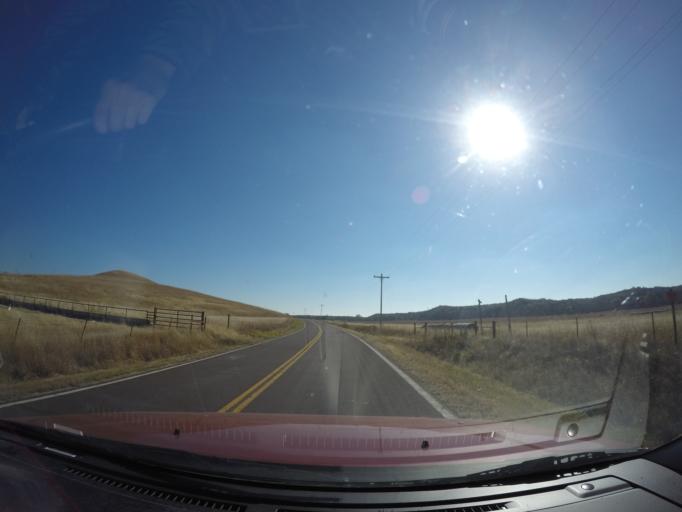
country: US
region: Kansas
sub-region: Geary County
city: Grandview Plaza
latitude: 38.9840
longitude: -96.7219
